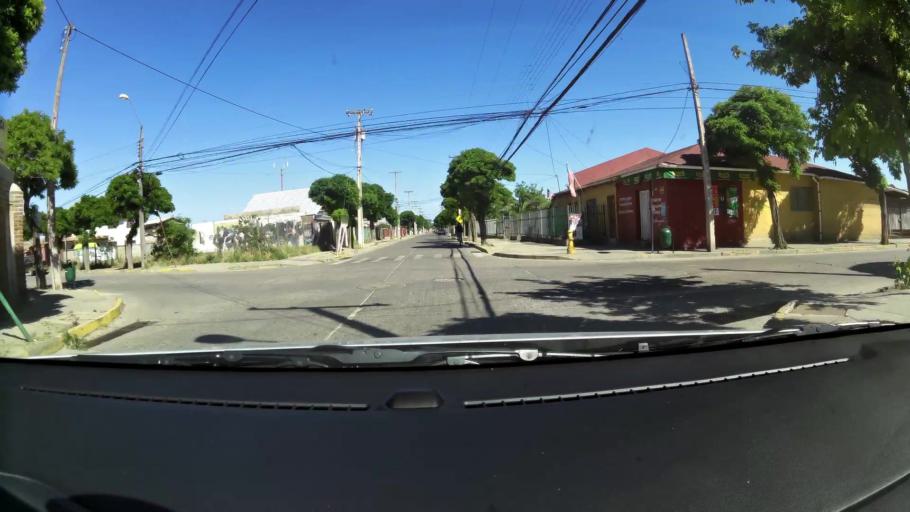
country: CL
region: Valparaiso
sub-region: Provincia de Marga Marga
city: Quilpue
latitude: -33.3219
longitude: -71.4013
